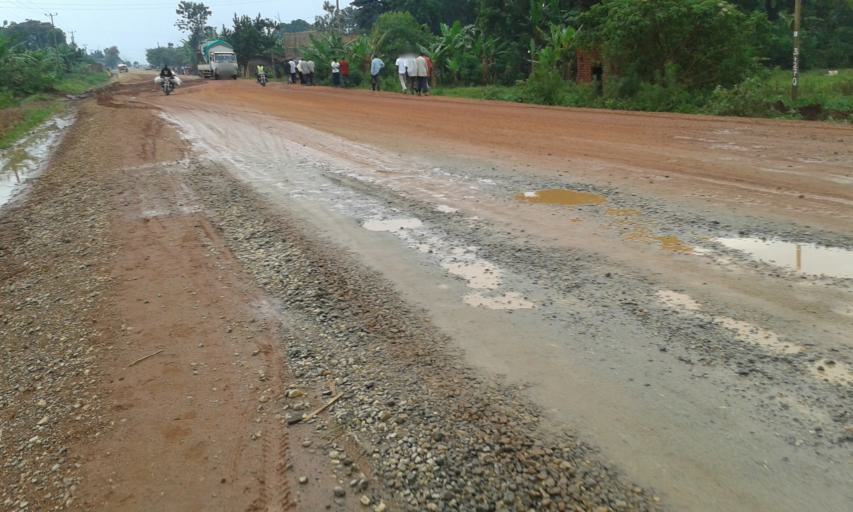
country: UG
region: Eastern Region
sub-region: Mbale District
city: Mbale
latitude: 1.1429
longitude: 34.1902
